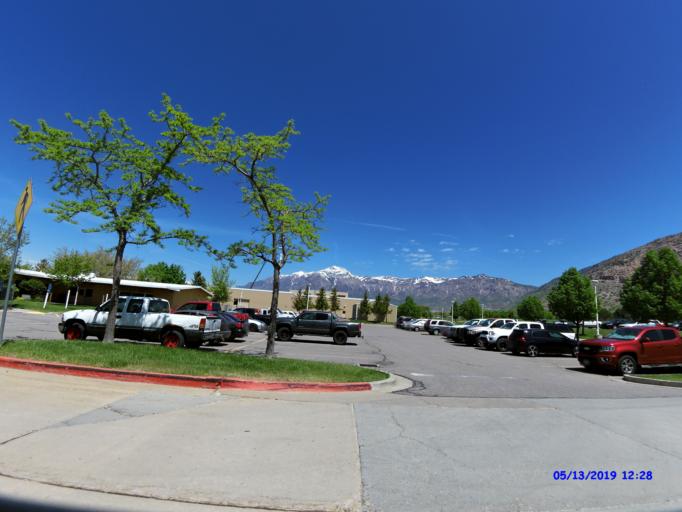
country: US
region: Utah
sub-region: Weber County
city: Harrisville
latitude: 41.2624
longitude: -111.9619
